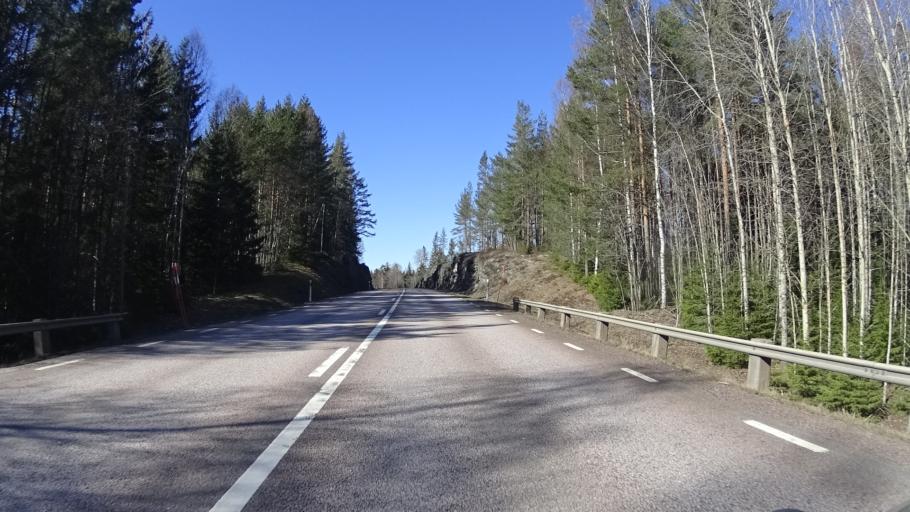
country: SE
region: Vaermland
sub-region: Karlstads Kommun
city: Edsvalla
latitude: 59.5932
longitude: 13.0088
